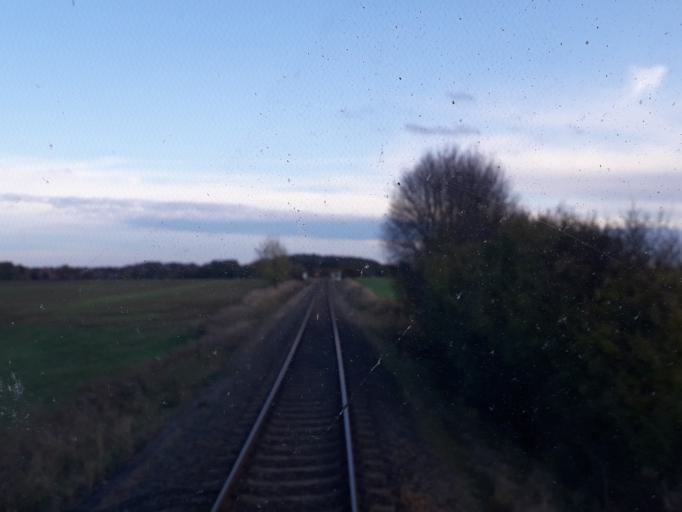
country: DE
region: Brandenburg
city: Wittstock
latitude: 53.1358
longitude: 12.4998
